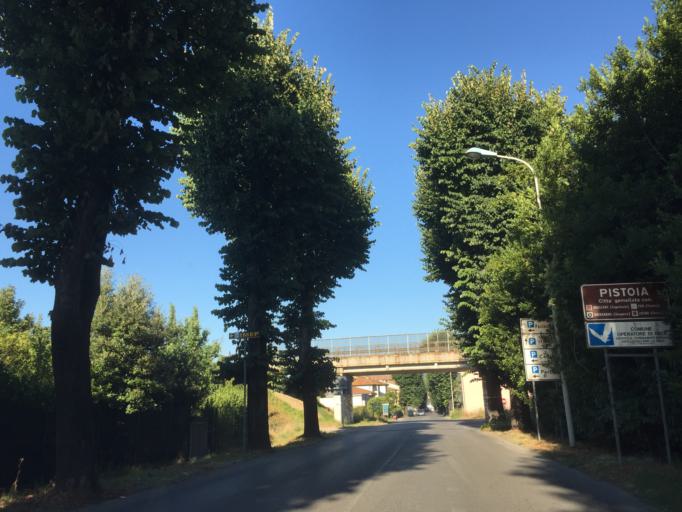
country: IT
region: Tuscany
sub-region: Provincia di Pistoia
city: Pistoia
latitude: 43.9408
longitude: 10.9351
